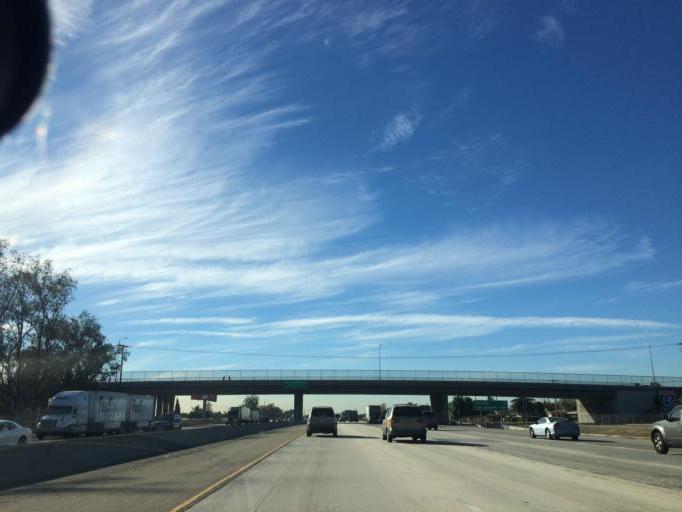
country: US
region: California
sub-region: San Bernardino County
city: Fontana
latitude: 34.0671
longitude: -117.4425
